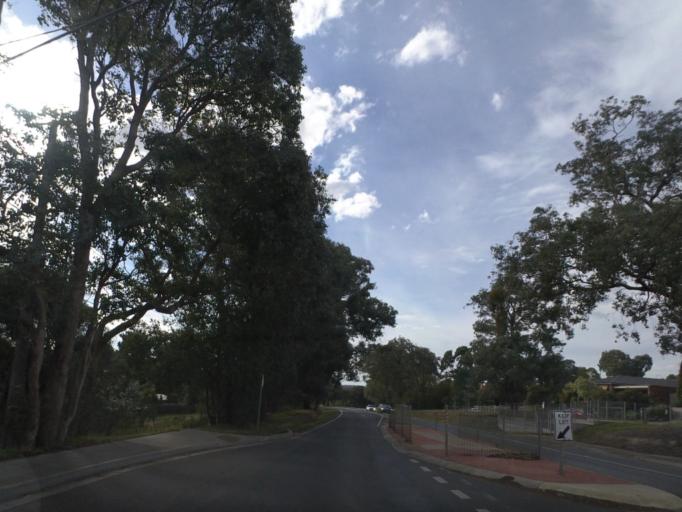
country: AU
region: Victoria
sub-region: Manningham
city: Donvale
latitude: -37.7587
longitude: 145.1737
